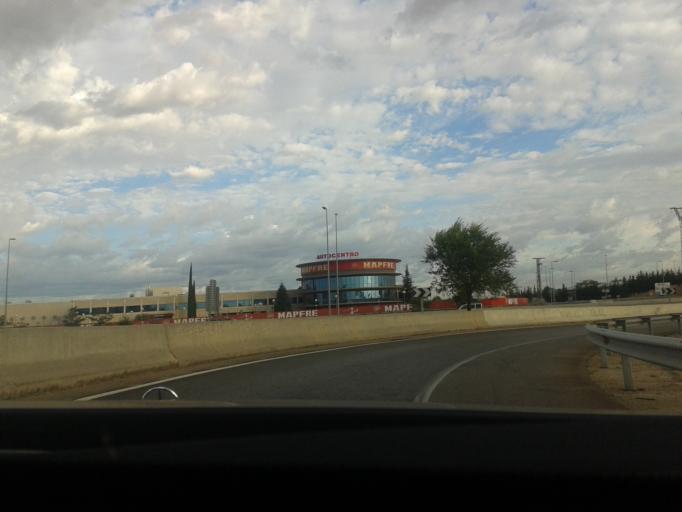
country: ES
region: Madrid
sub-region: Provincia de Madrid
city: Alcala de Henares
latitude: 40.4910
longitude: -3.3895
